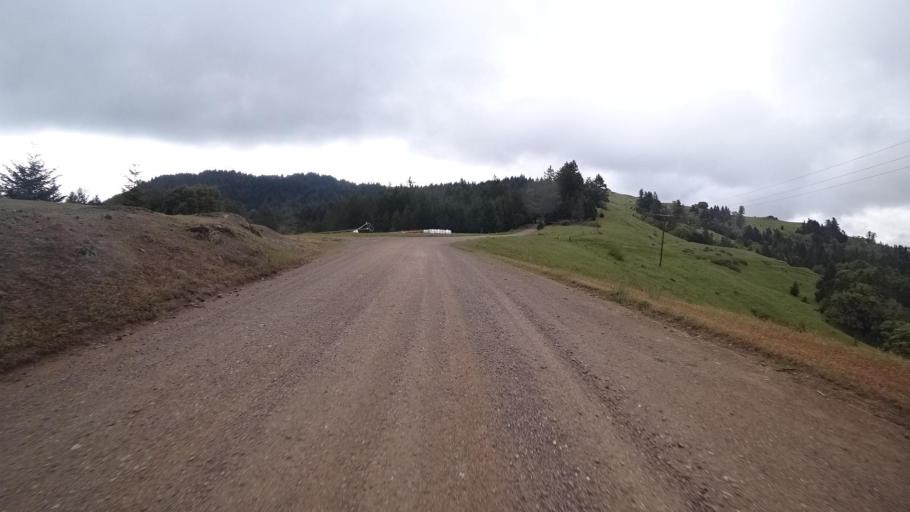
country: US
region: California
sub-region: Humboldt County
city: Redway
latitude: 40.2177
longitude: -123.7538
